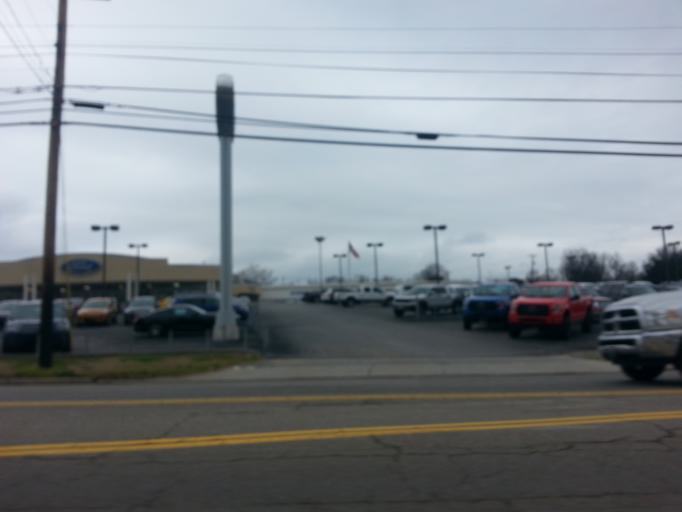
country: US
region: Tennessee
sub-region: Hamblen County
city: Morristown
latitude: 36.2066
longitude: -83.3032
